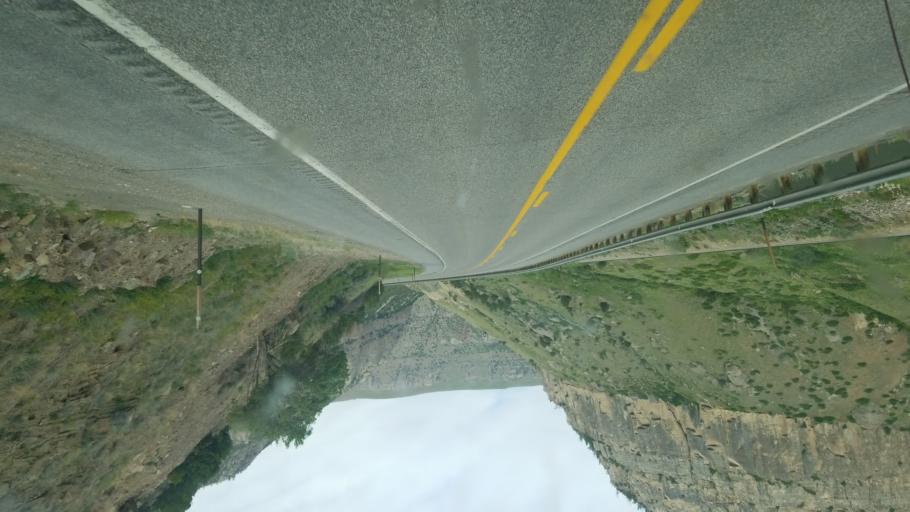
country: US
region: Wyoming
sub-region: Hot Springs County
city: Thermopolis
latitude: 43.5022
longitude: -108.1639
